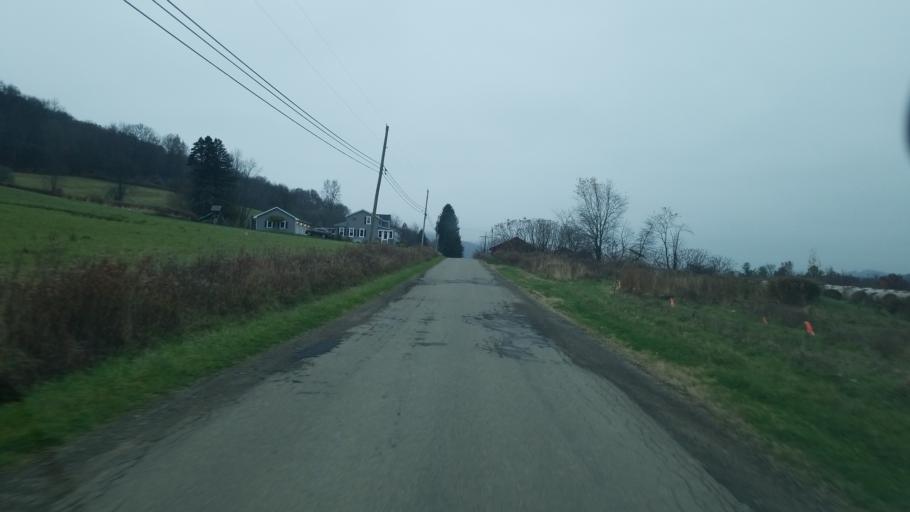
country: US
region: Pennsylvania
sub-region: McKean County
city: Smethport
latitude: 41.7883
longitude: -78.4262
